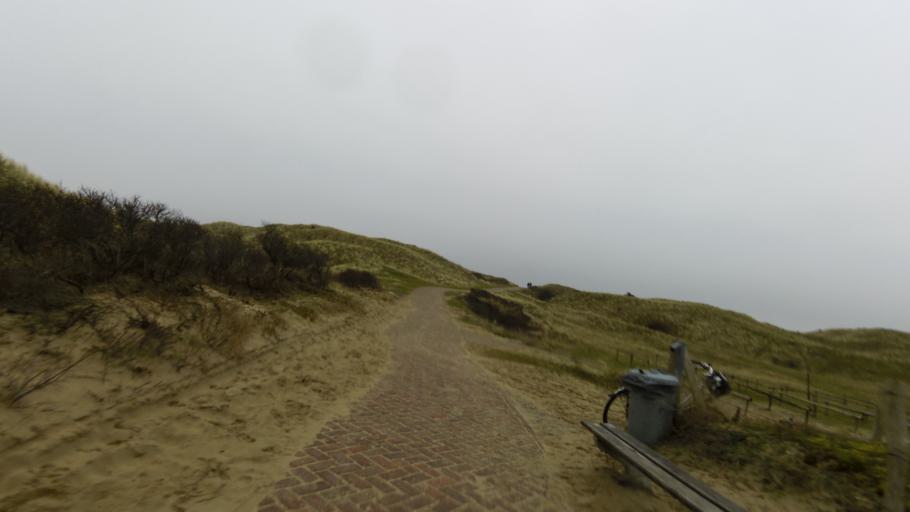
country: NL
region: North Holland
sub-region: Gemeente Castricum
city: Castricum
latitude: 52.5474
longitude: 4.6065
